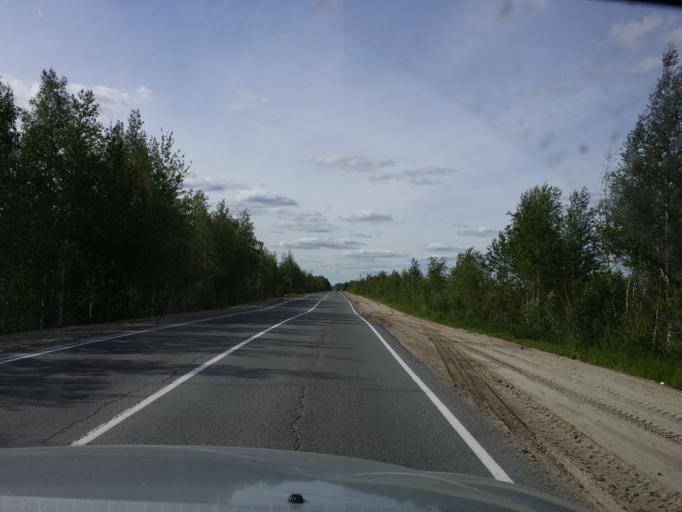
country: RU
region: Khanty-Mansiyskiy Avtonomnyy Okrug
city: Nizhnevartovsk
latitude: 61.1075
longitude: 76.6116
